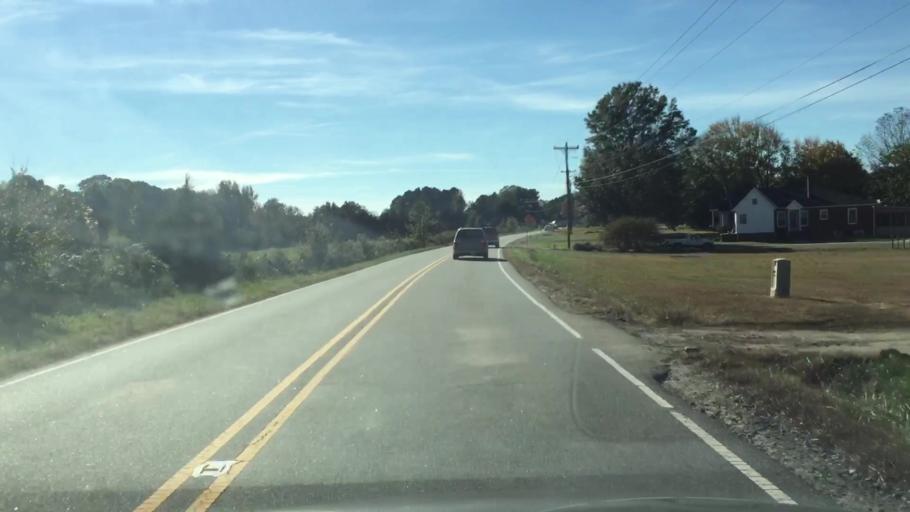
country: US
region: North Carolina
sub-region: Iredell County
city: Mooresville
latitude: 35.5995
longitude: -80.7588
